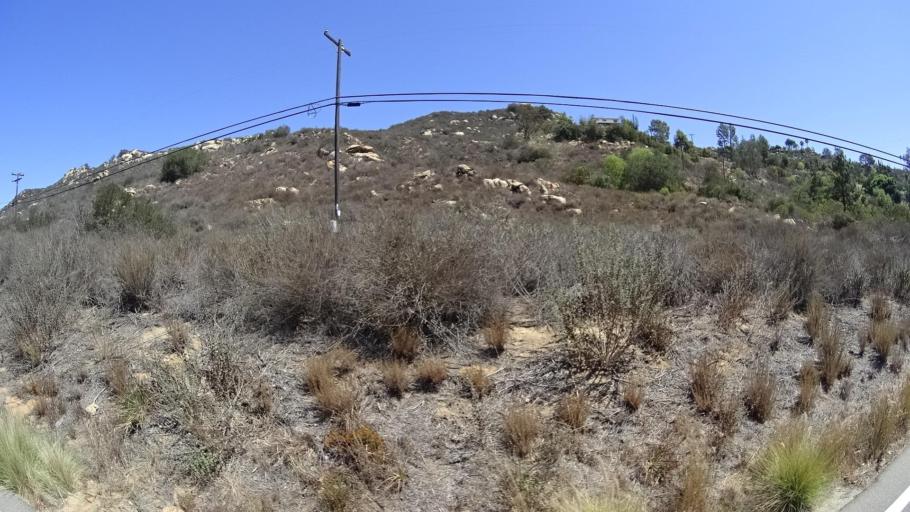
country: US
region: California
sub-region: San Diego County
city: Rainbow
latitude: 33.4027
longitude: -117.1387
